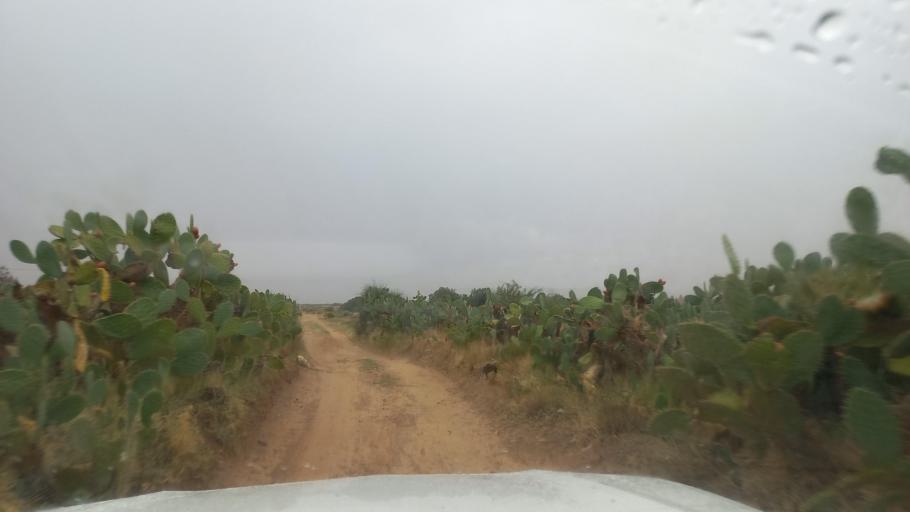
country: TN
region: Al Qasrayn
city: Kasserine
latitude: 35.2707
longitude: 8.9453
